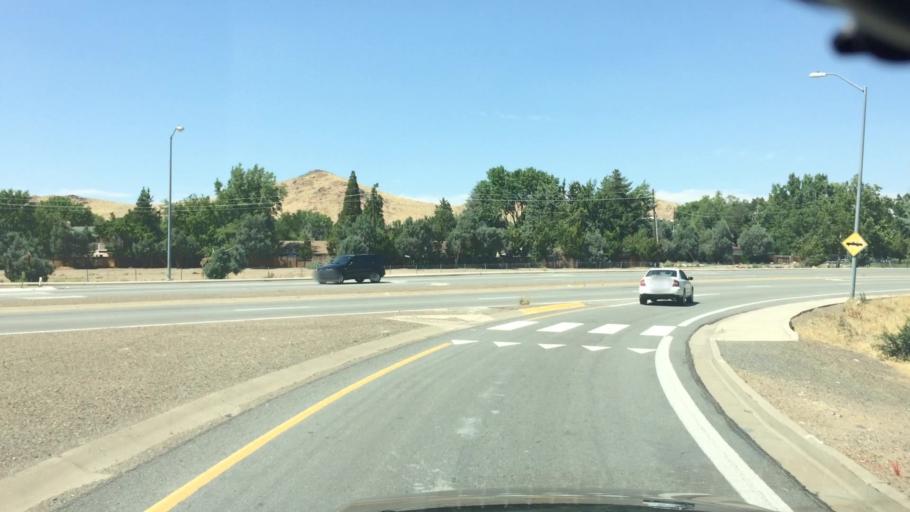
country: US
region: Nevada
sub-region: Washoe County
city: Sparks
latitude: 39.5553
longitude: -119.7347
